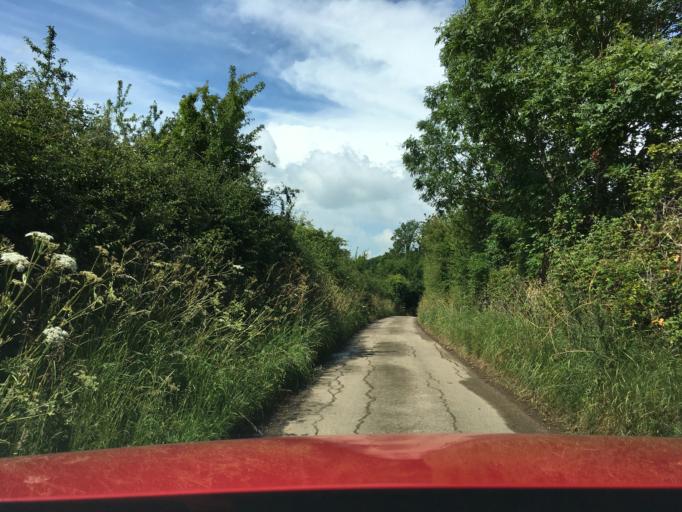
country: GB
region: England
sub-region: Gloucestershire
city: Tetbury
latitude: 51.6421
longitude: -2.1757
